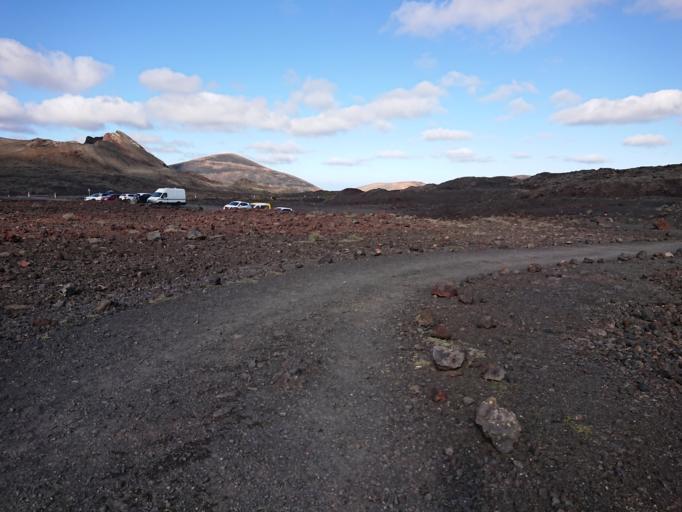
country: ES
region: Canary Islands
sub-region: Provincia de Las Palmas
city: Tias
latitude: 29.0043
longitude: -13.6831
